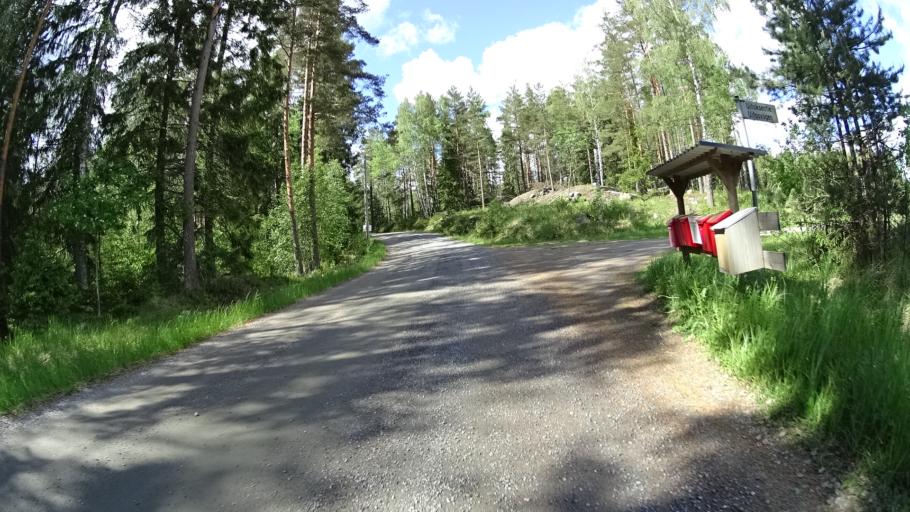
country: FI
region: Uusimaa
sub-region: Raaseporin
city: Pohja
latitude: 60.1808
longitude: 23.5862
